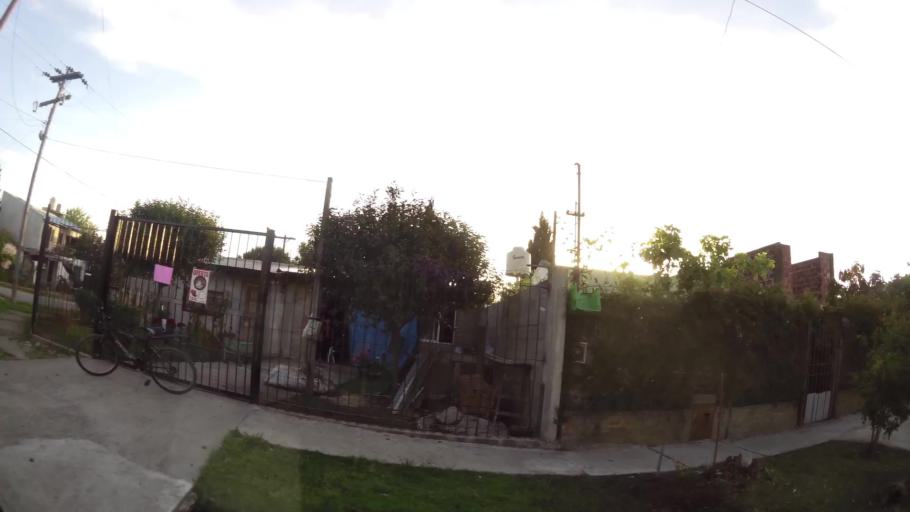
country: AR
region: Buenos Aires
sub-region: Partido de Quilmes
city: Quilmes
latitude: -34.7846
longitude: -58.2177
